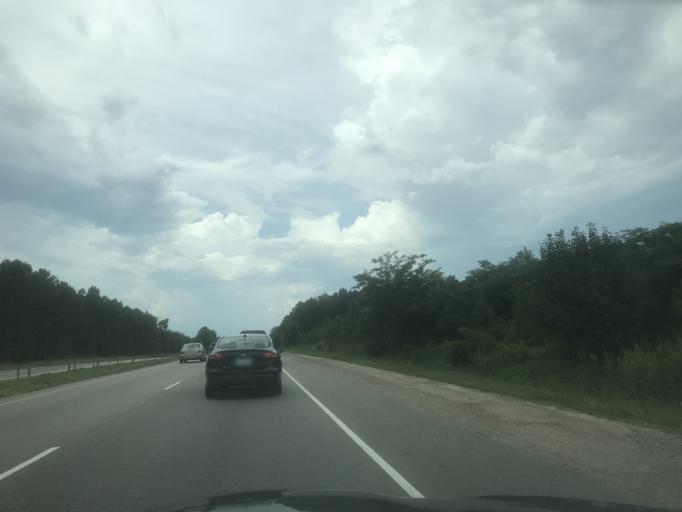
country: US
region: North Carolina
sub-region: Johnston County
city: Clayton
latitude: 35.6770
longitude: -78.5223
